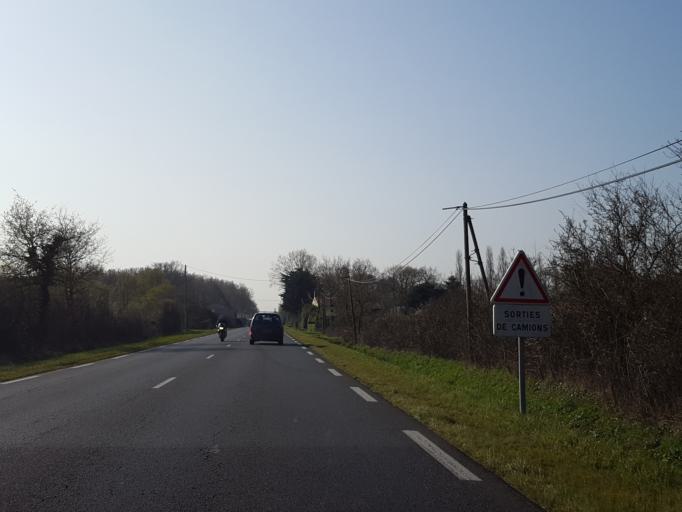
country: FR
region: Pays de la Loire
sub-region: Departement de la Loire-Atlantique
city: Geneston
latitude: 47.0754
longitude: -1.5223
